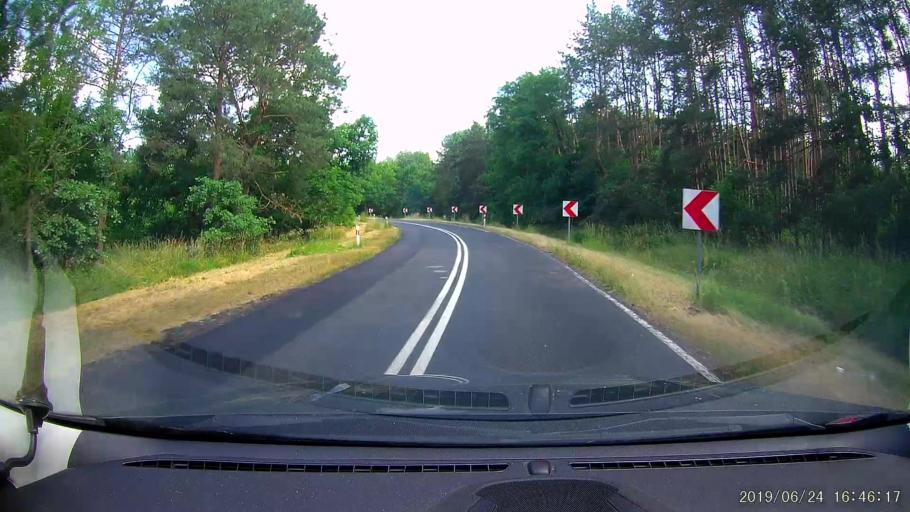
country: PL
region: Lublin Voivodeship
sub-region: Powiat tomaszowski
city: Laszczow
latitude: 50.5267
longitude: 23.6759
